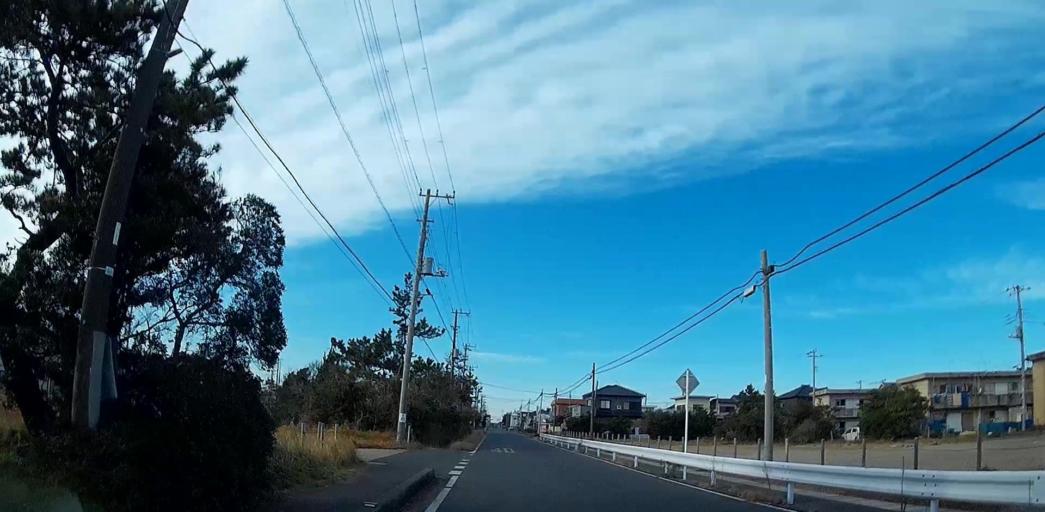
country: JP
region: Chiba
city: Hasaki
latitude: 35.7447
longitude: 140.8378
